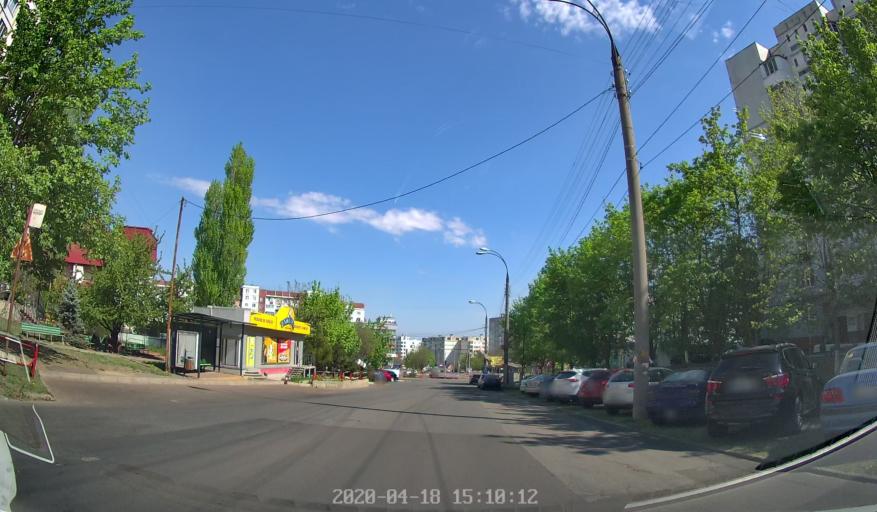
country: MD
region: Chisinau
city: Chisinau
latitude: 47.0438
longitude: 28.8887
